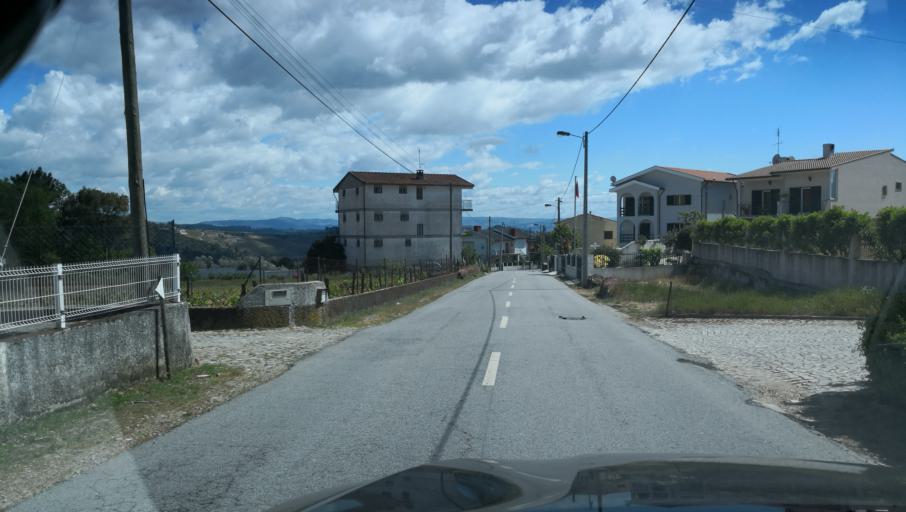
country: PT
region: Vila Real
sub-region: Vila Real
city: Vila Real
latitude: 41.2638
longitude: -7.7305
